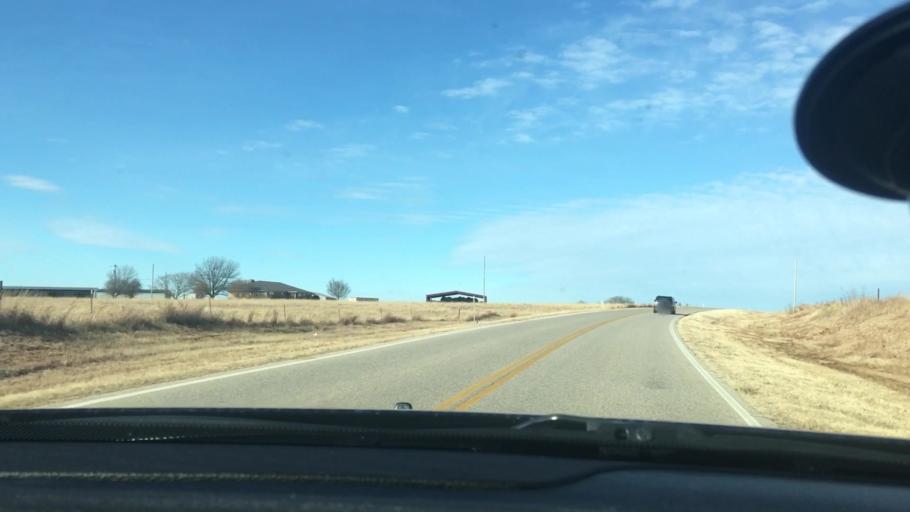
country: US
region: Oklahoma
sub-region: Garvin County
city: Stratford
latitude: 34.9864
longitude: -97.0413
